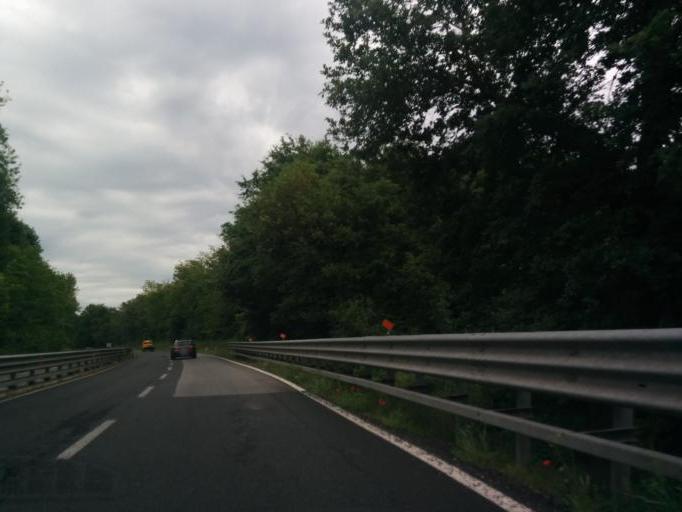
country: IT
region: Tuscany
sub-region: Provincia di Siena
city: Castellina Scalo
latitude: 43.3956
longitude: 11.2022
